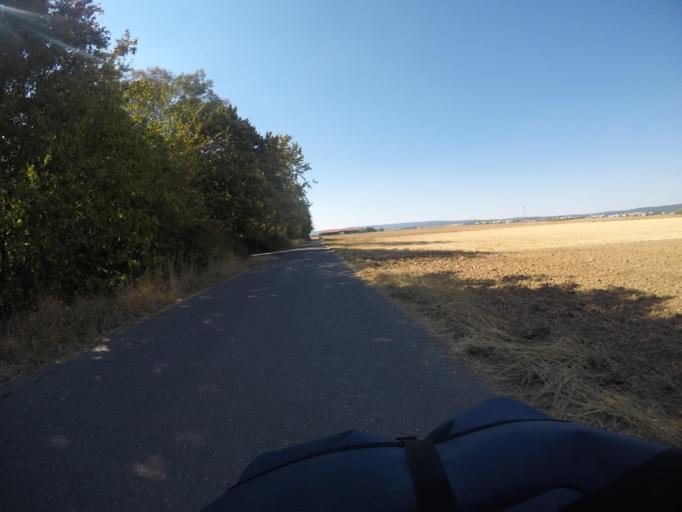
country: DE
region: Hesse
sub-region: Regierungsbezirk Darmstadt
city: Hochheim am Main
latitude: 50.0347
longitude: 8.3465
